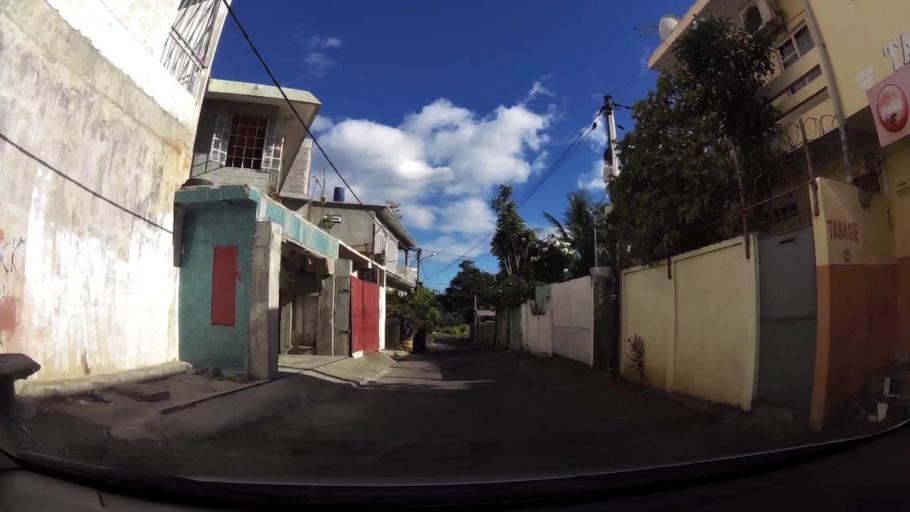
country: MU
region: Pamplemousses
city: Le Hochet
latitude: -20.1499
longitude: 57.5153
